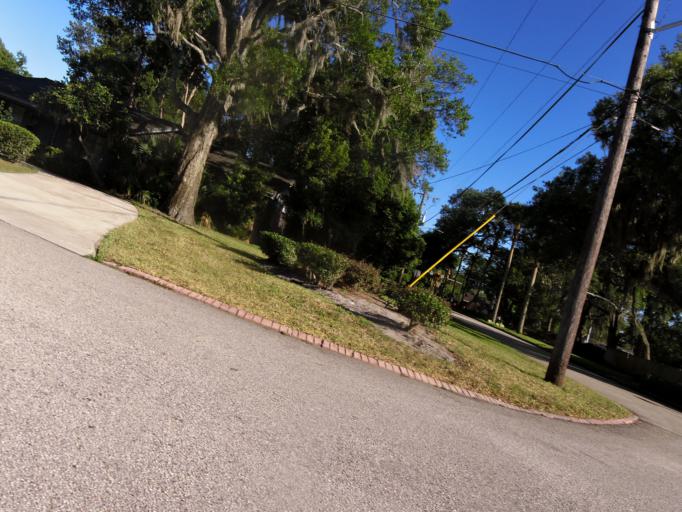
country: US
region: Florida
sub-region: Duval County
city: Jacksonville
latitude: 30.3106
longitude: -81.6143
